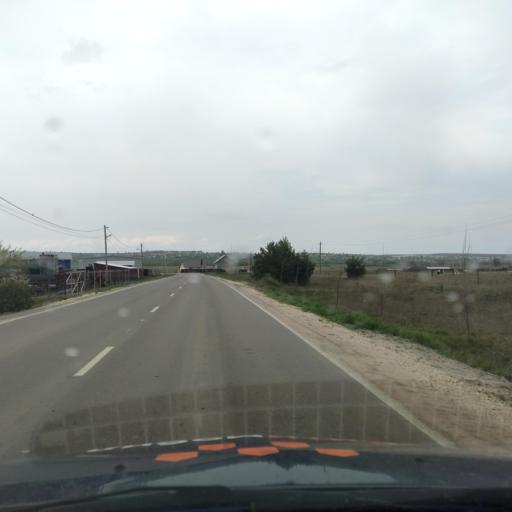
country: RU
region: Voronezj
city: Podgornoye
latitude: 51.8529
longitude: 39.1538
